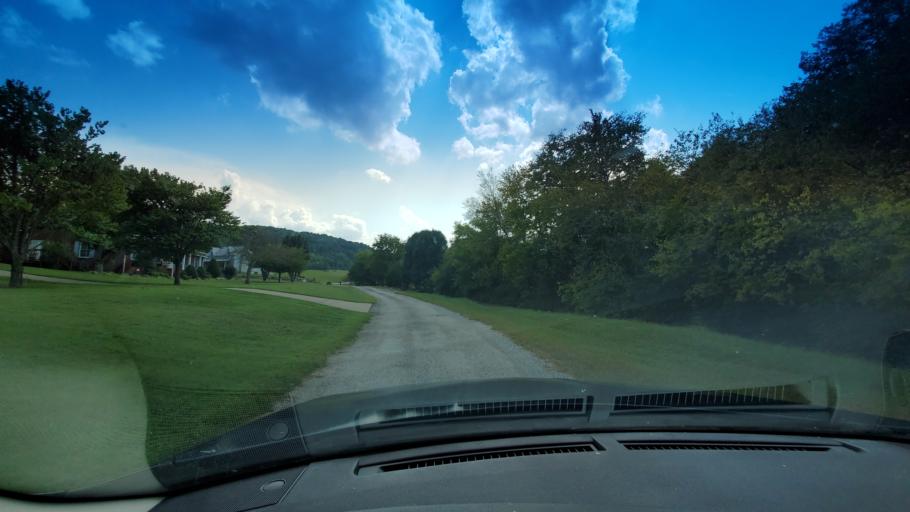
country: US
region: Tennessee
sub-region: Smith County
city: South Carthage
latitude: 36.2273
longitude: -85.9812
